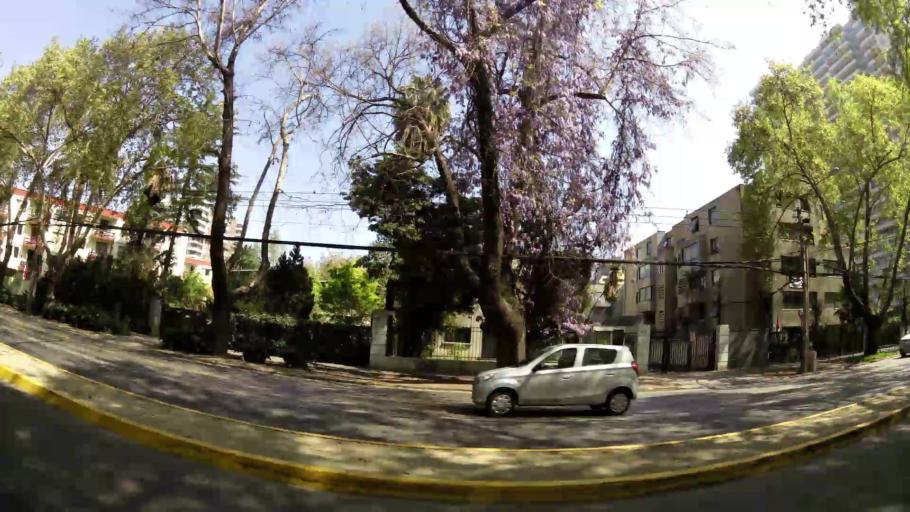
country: CL
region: Santiago Metropolitan
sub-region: Provincia de Santiago
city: Villa Presidente Frei, Nunoa, Santiago, Chile
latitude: -33.4611
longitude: -70.5981
